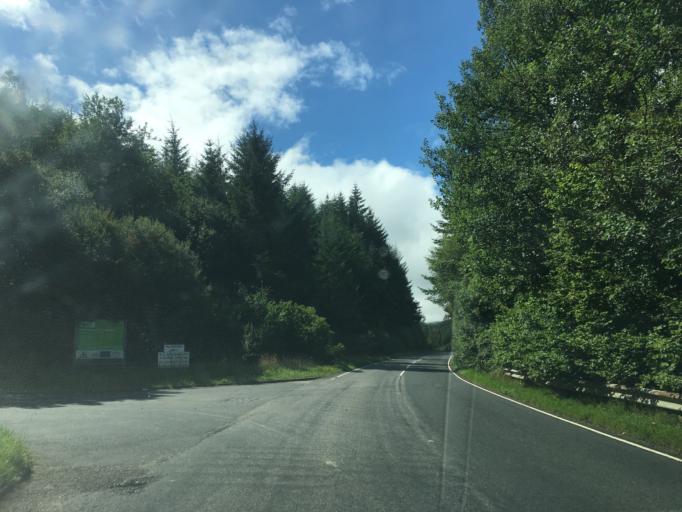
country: GB
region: Scotland
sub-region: Argyll and Bute
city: Dunoon
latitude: 55.9941
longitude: -4.9810
